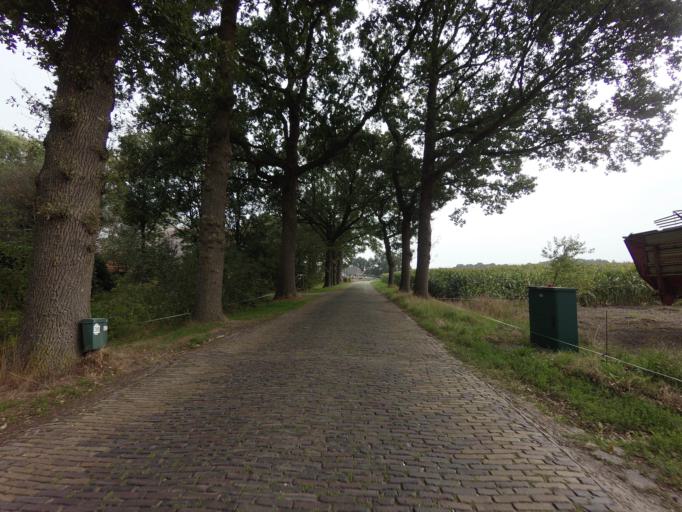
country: NL
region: Drenthe
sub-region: Gemeente Westerveld
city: Dwingeloo
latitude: 52.8686
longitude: 6.4268
